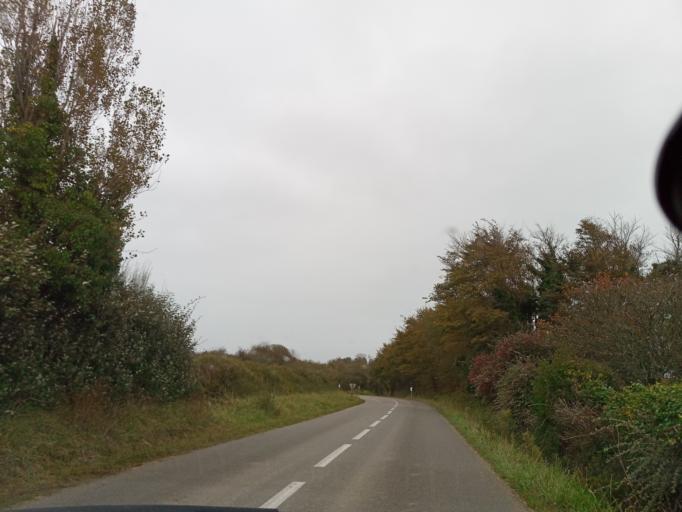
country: FR
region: Brittany
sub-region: Departement du Finistere
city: Esquibien
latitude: 48.0192
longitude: -4.5636
